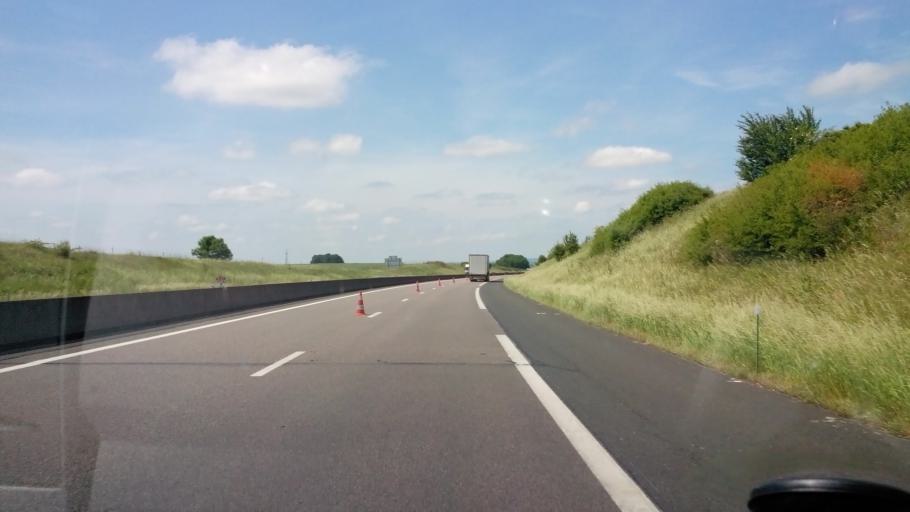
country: FR
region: Lorraine
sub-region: Departement des Vosges
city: Bulgneville
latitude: 48.2273
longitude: 5.8554
